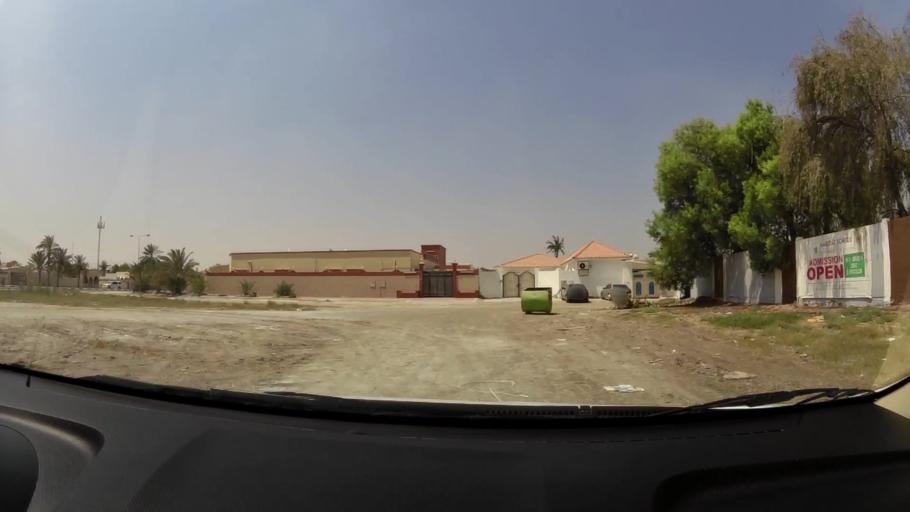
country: AE
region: Umm al Qaywayn
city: Umm al Qaywayn
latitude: 25.5562
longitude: 55.5551
